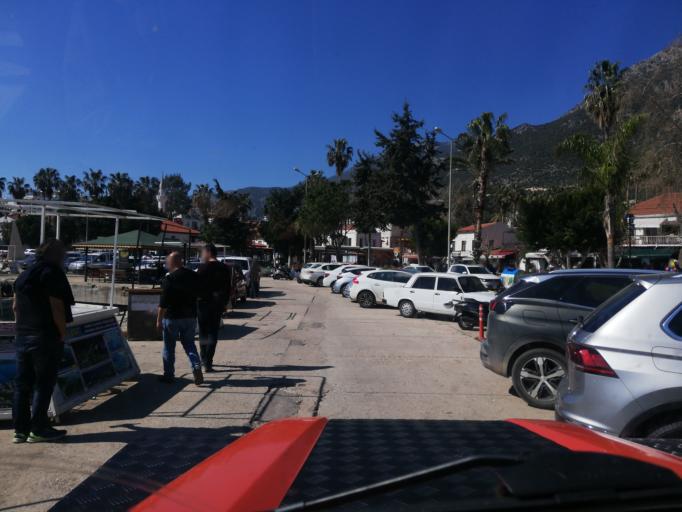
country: TR
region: Antalya
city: Kas
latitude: 36.1989
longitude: 29.6414
